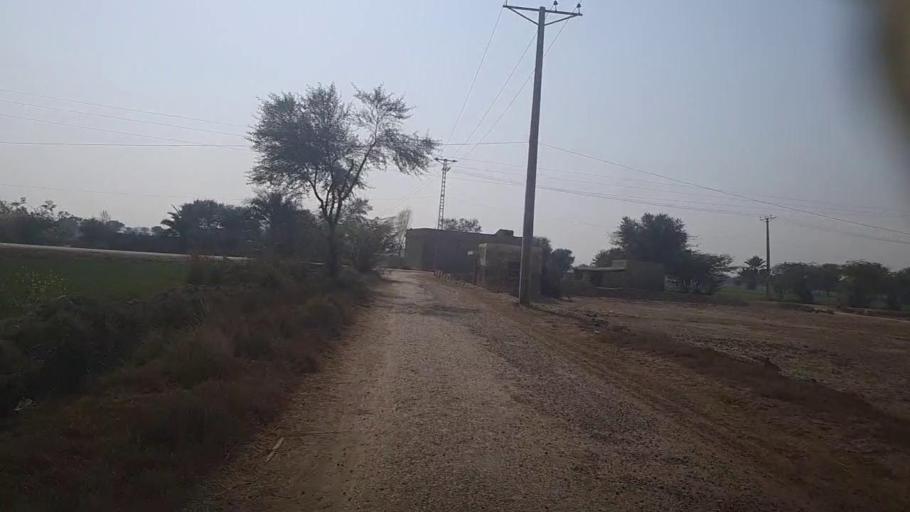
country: PK
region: Sindh
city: Kot Diji
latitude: 27.3467
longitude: 68.7304
